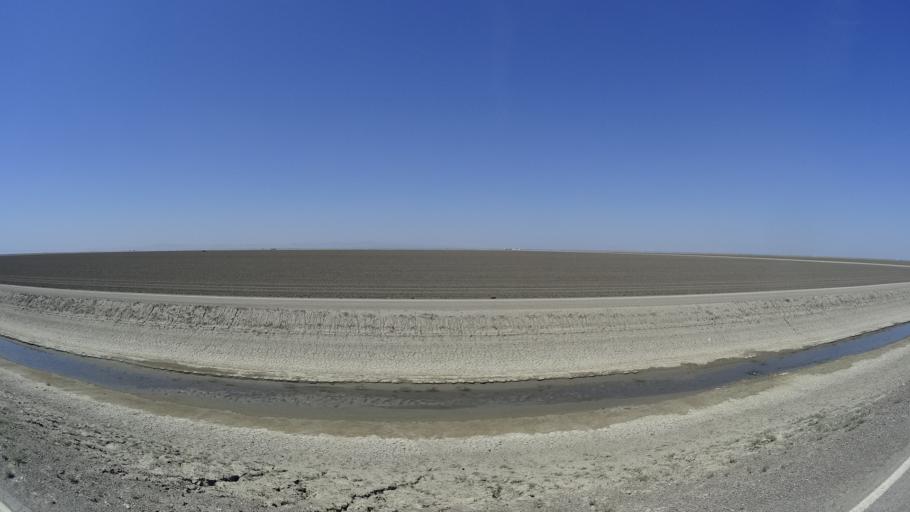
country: US
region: California
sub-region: Kings County
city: Corcoran
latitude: 36.0125
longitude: -119.6433
